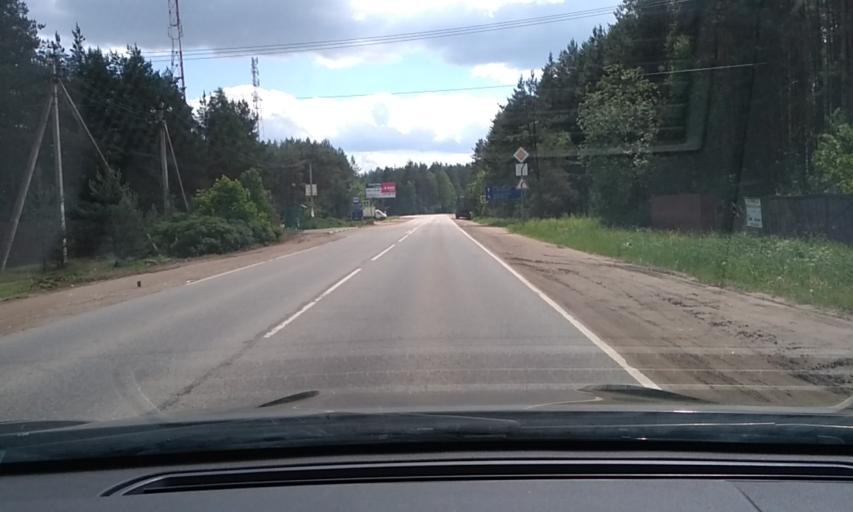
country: RU
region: Leningrad
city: Imeni Sverdlova
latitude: 59.8606
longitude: 30.6714
